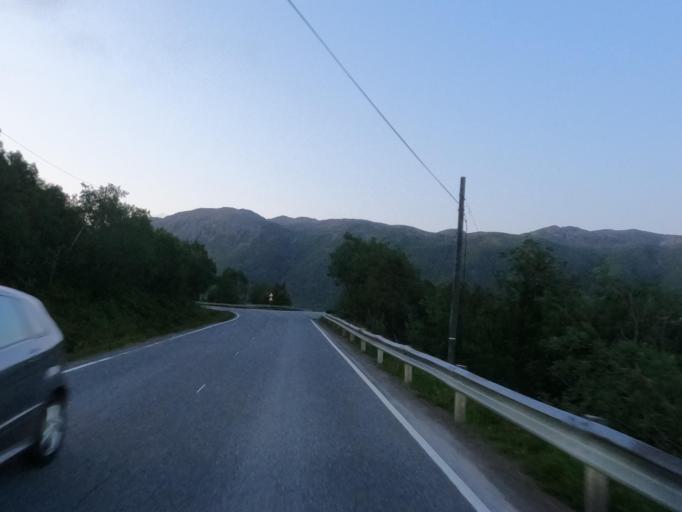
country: NO
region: Nordland
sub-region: Lodingen
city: Lodingen
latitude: 68.5637
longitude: 15.7976
